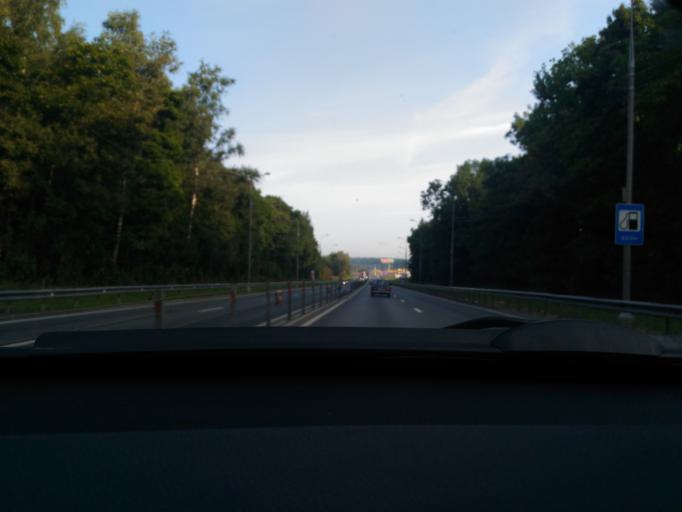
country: RU
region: Moskovskaya
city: Marfino
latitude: 56.0366
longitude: 37.5429
